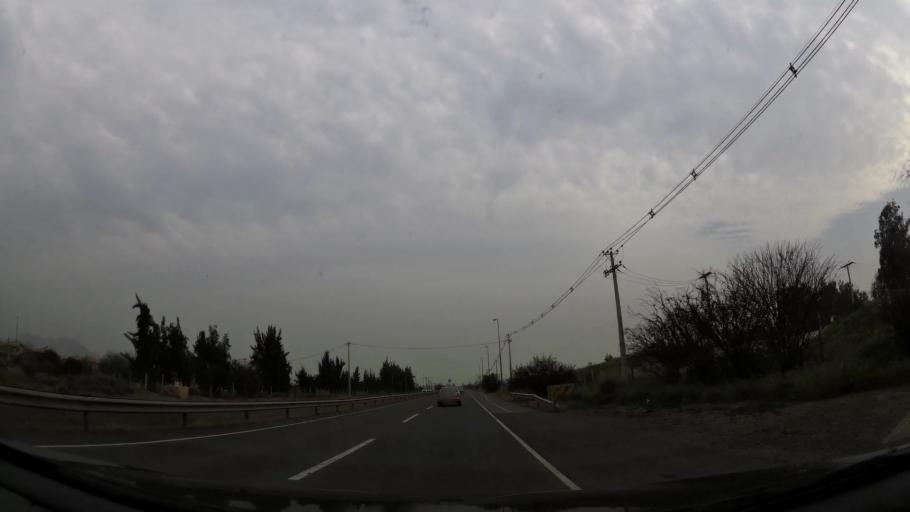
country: CL
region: Santiago Metropolitan
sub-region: Provincia de Chacabuco
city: Chicureo Abajo
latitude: -33.2156
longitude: -70.6744
